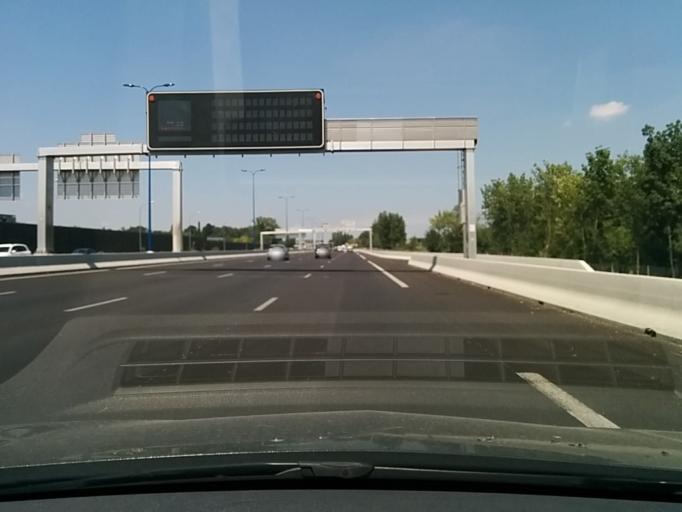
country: FR
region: Midi-Pyrenees
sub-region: Departement de la Haute-Garonne
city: Ramonville-Saint-Agne
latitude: 43.5644
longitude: 1.4859
